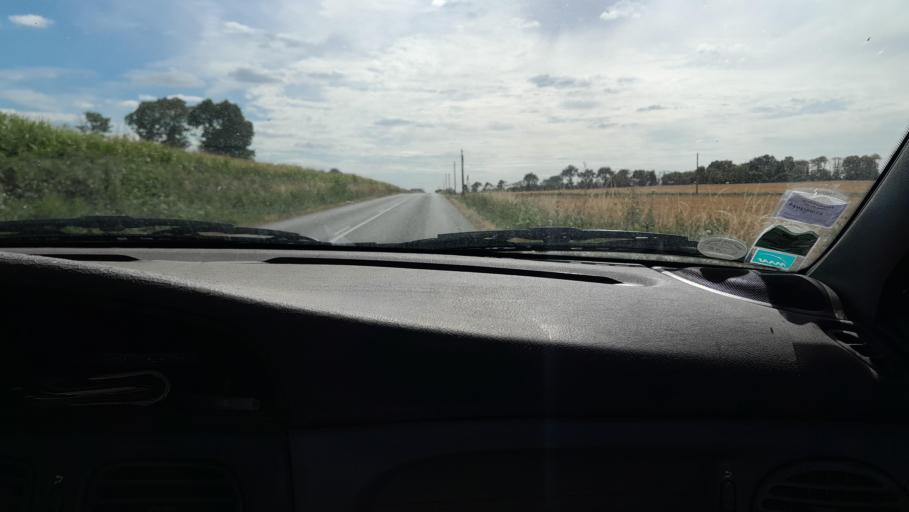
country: FR
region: Pays de la Loire
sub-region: Departement de la Mayenne
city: Loiron
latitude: 48.0199
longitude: -0.9313
